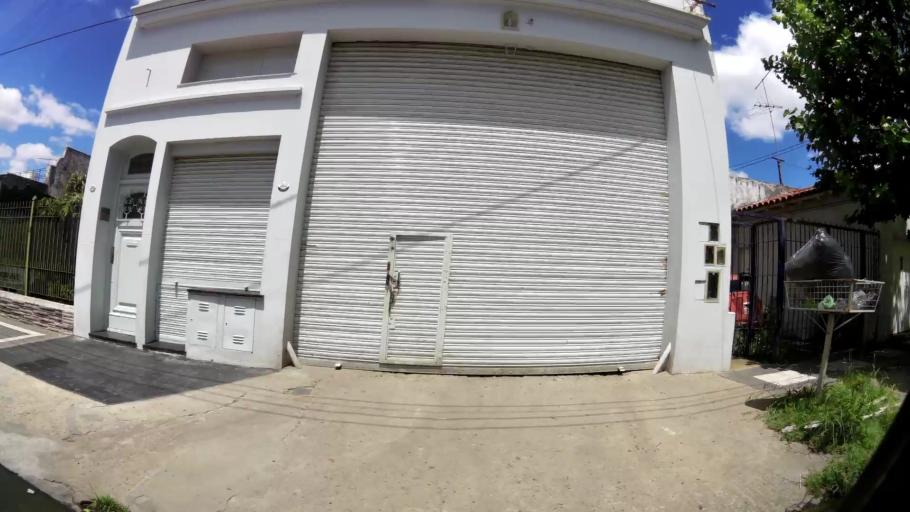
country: AR
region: Buenos Aires
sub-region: Partido de Lanus
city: Lanus
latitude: -34.7279
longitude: -58.4098
